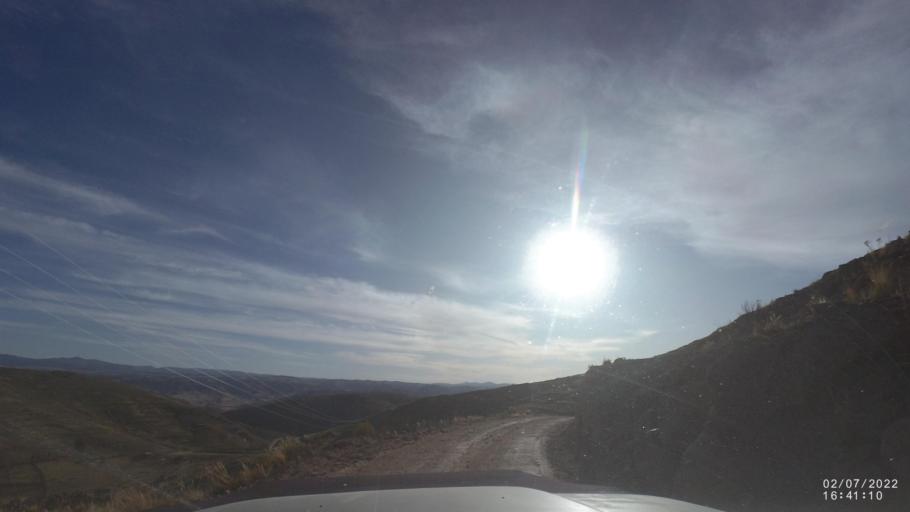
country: BO
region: Cochabamba
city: Irpa Irpa
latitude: -17.9726
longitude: -66.5001
